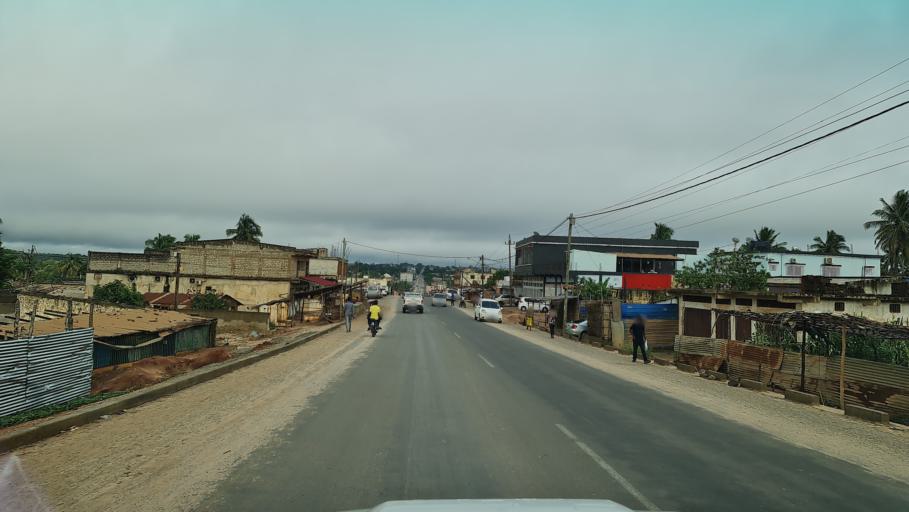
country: MZ
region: Nampula
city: Nampula
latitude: -15.1344
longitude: 39.2758
